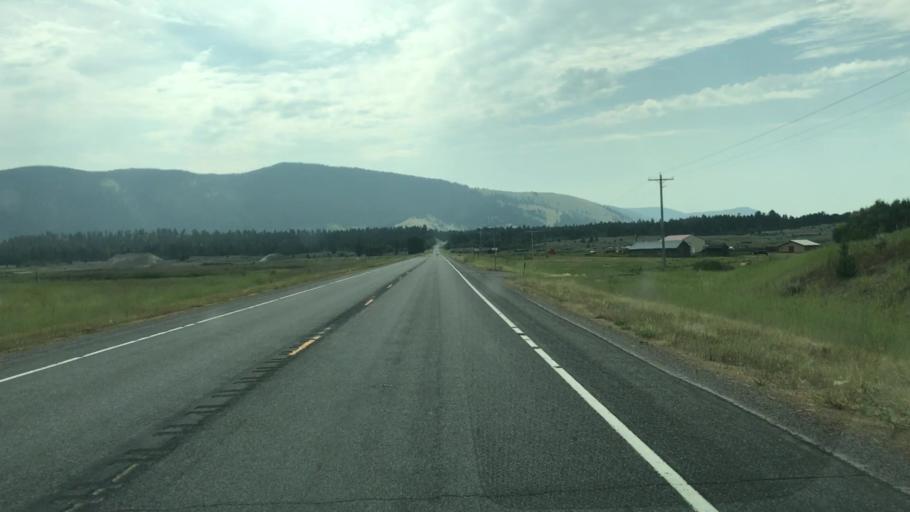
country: US
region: Montana
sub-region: Lewis and Clark County
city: Lincoln
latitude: 46.9890
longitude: -113.0113
